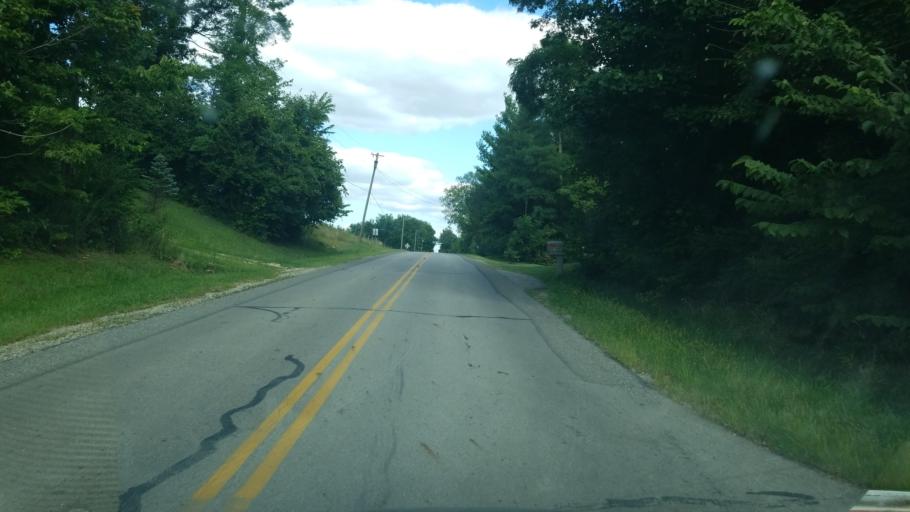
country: US
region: Ohio
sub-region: Champaign County
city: Saint Paris
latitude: 40.1582
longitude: -83.9204
